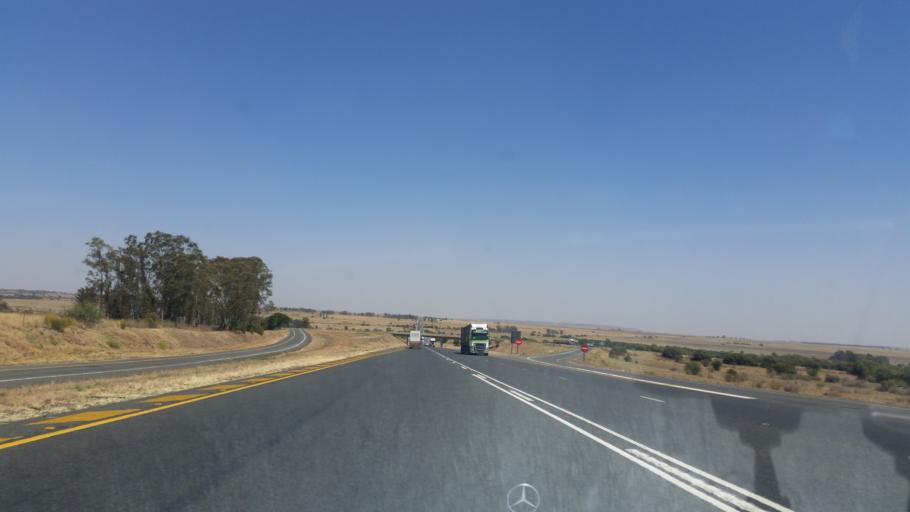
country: ZA
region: Orange Free State
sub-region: Lejweleputswa District Municipality
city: Winburg
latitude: -28.6248
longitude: 26.9138
